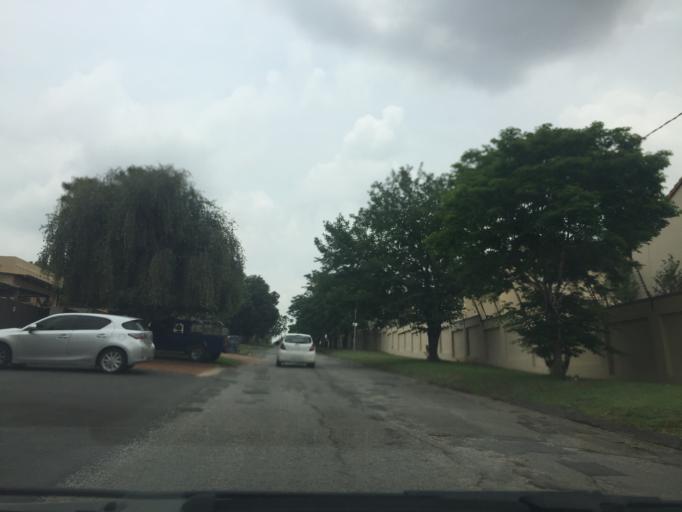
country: ZA
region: Gauteng
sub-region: City of Johannesburg Metropolitan Municipality
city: Diepsloot
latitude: -26.0148
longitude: 27.9950
